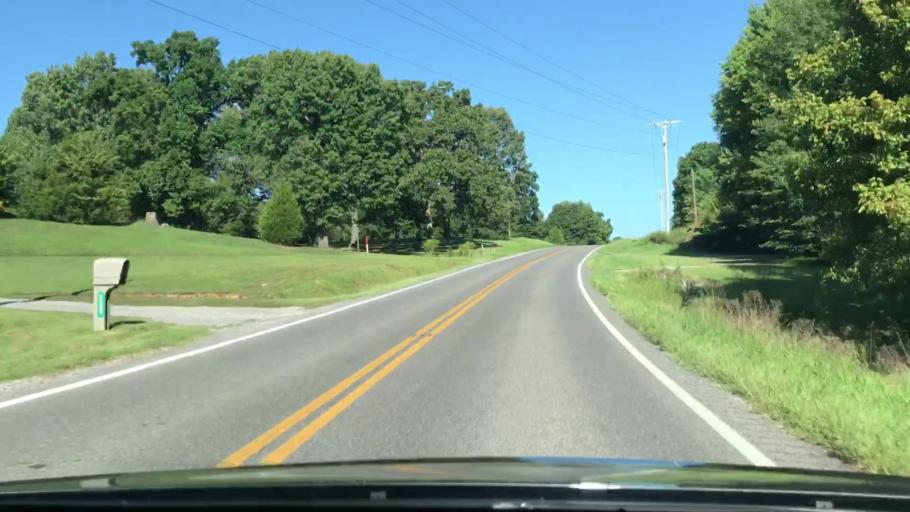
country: US
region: Kentucky
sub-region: Graves County
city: Mayfield
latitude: 36.7741
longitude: -88.5035
